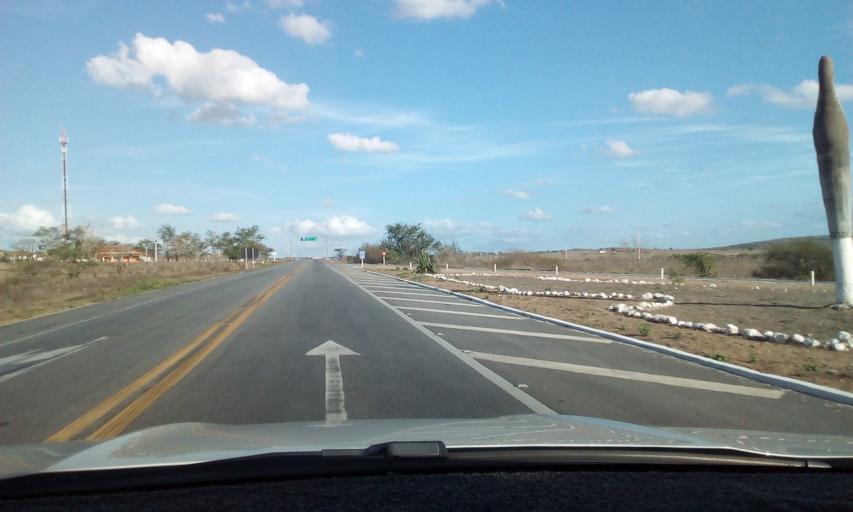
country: BR
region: Paraiba
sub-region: Pocinhos
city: Pocinhos
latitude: -7.1520
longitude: -36.1078
